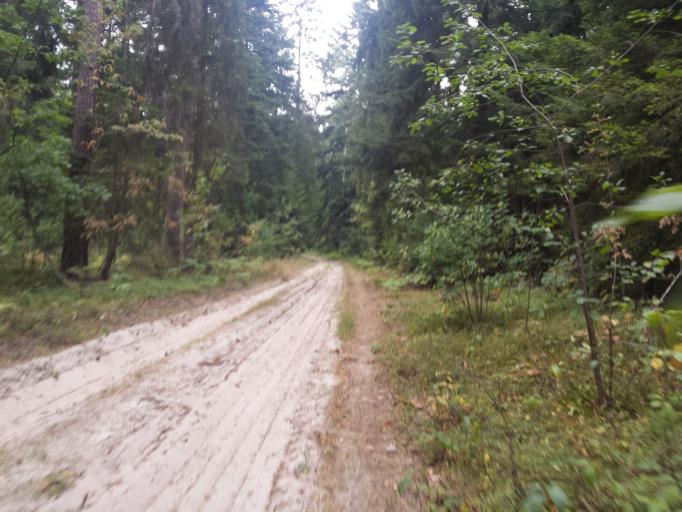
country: PL
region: Swietokrzyskie
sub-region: Powiat staszowski
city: Bogoria
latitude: 50.6558
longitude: 21.1703
